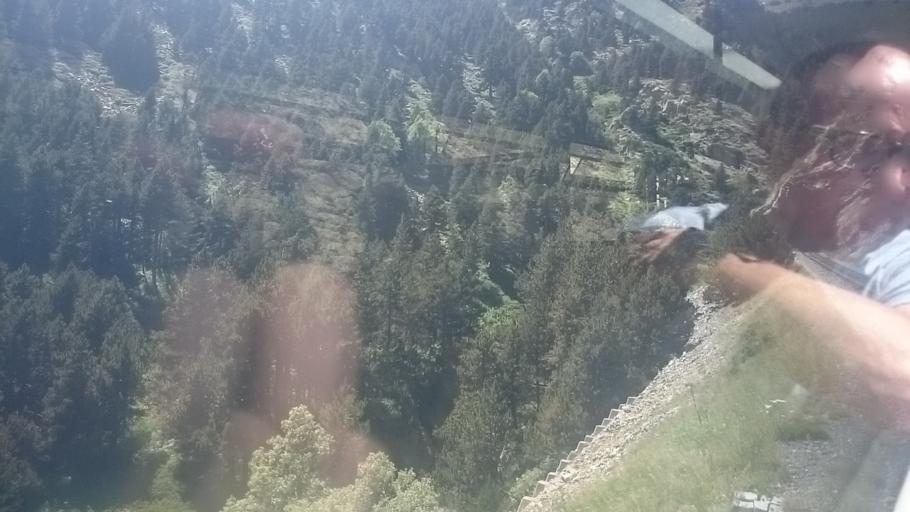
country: ES
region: Catalonia
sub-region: Provincia de Girona
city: Ribes de Freser
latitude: 42.3876
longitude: 2.1578
